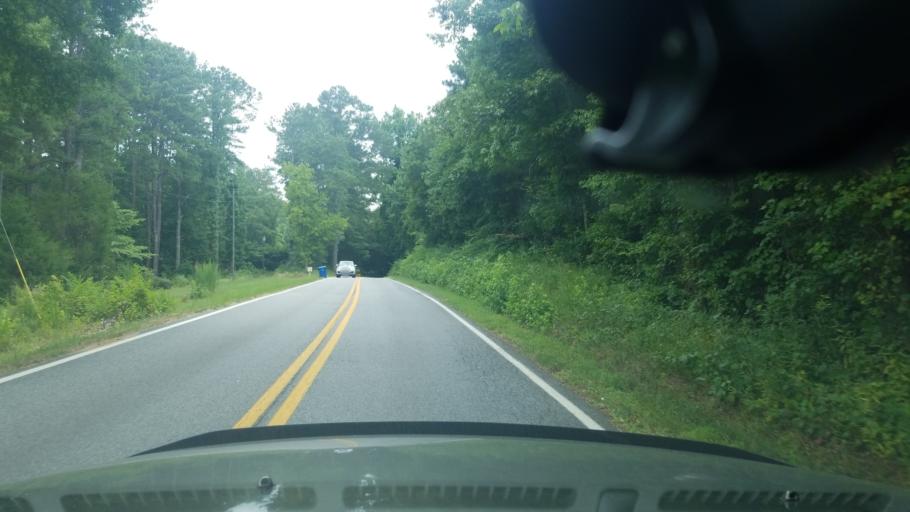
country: US
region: Georgia
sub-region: Fulton County
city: Milton
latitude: 34.1503
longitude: -84.2427
